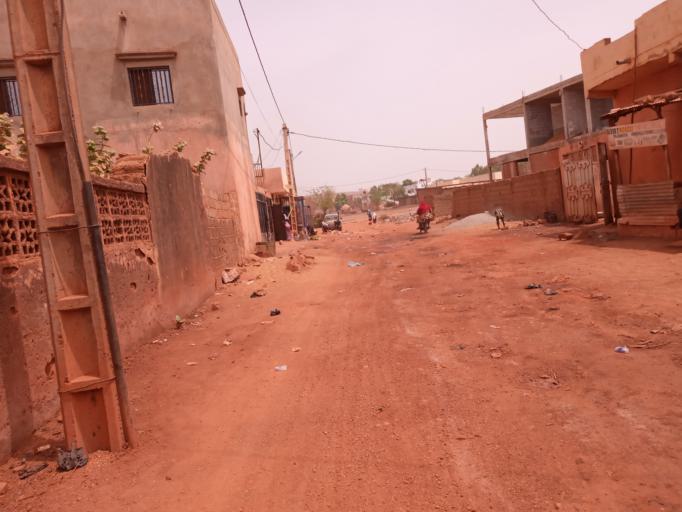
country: ML
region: Bamako
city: Bamako
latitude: 12.6733
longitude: -7.9103
